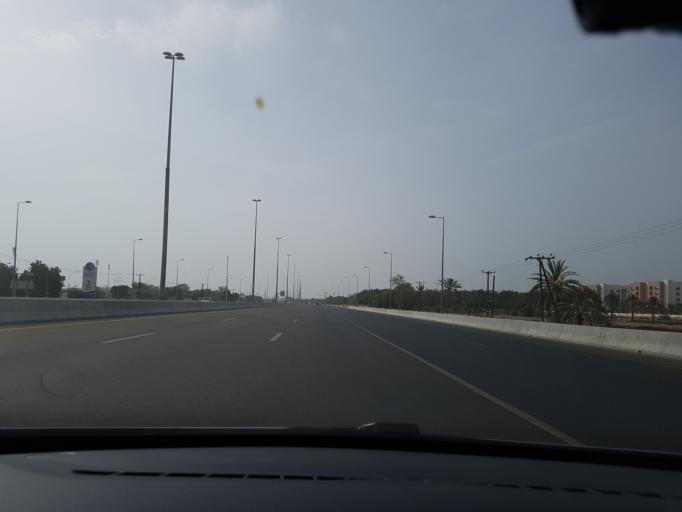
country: OM
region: Al Batinah
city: Al Sohar
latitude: 24.3366
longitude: 56.7361
